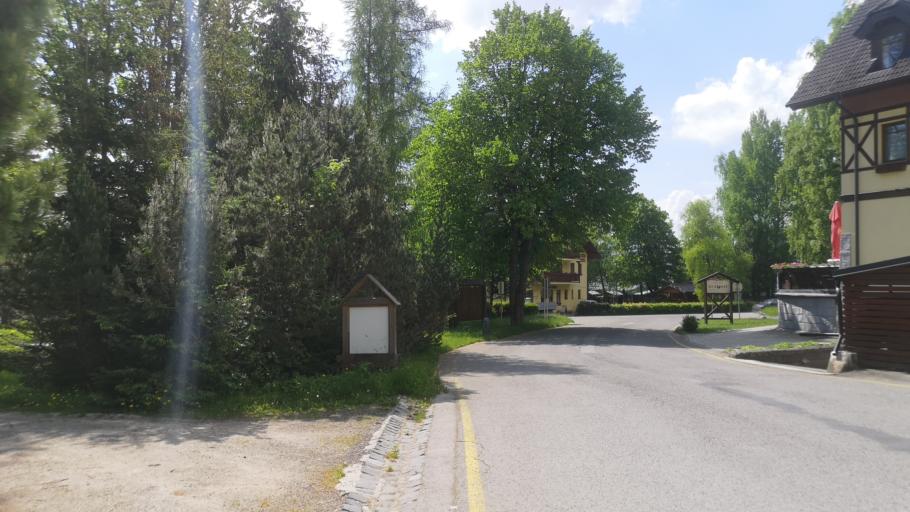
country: SK
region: Presovsky
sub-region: Okres Poprad
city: Nova Lesna
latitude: 49.1662
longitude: 20.2782
